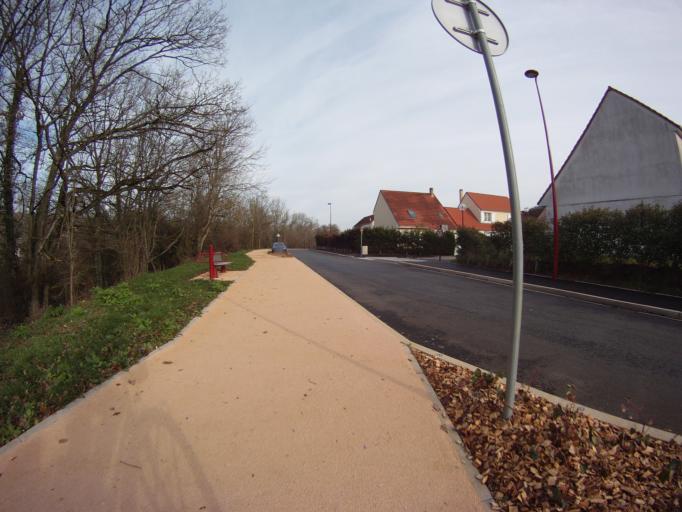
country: FR
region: Lorraine
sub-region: Departement de Meurthe-et-Moselle
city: Champigneulles
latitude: 48.7222
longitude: 6.1488
